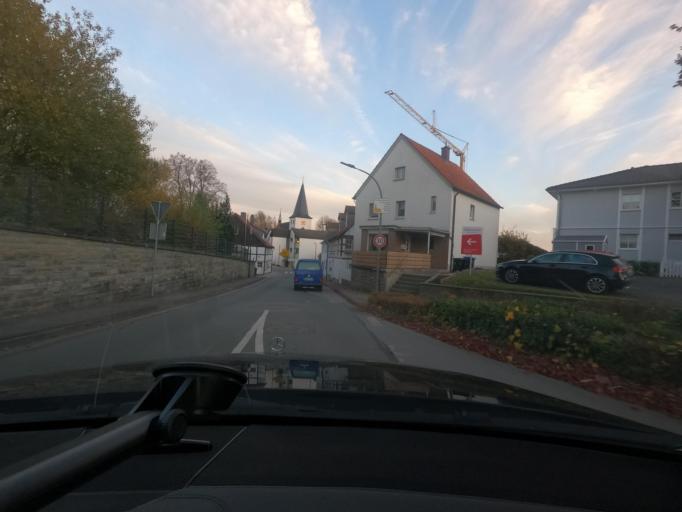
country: DE
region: North Rhine-Westphalia
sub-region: Regierungsbezirk Arnsberg
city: Mohnesee
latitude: 51.4979
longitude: 8.1277
